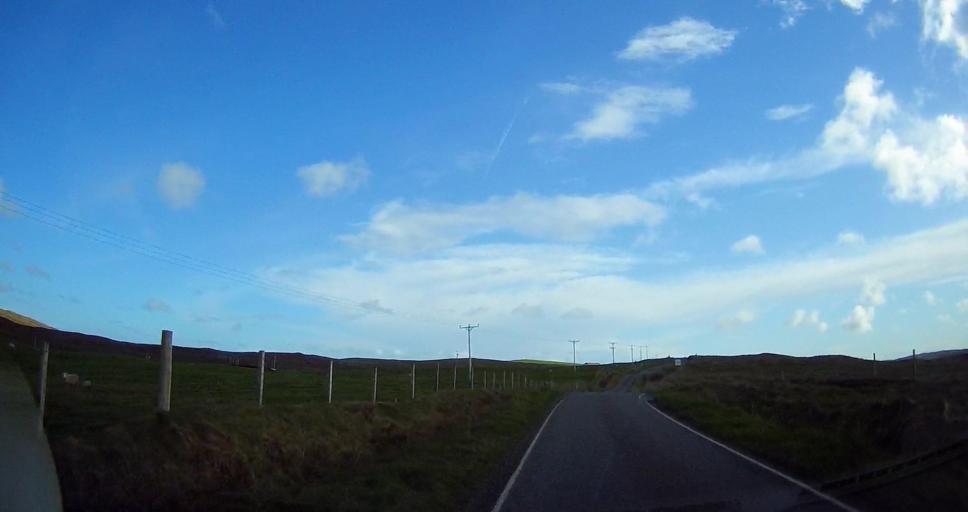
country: GB
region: Scotland
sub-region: Shetland Islands
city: Shetland
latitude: 60.3658
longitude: -1.1416
